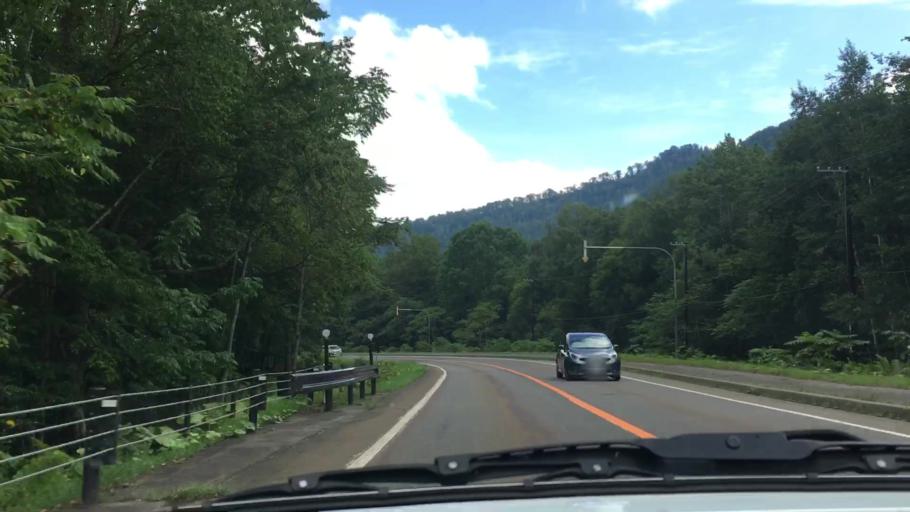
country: JP
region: Hokkaido
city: Otofuke
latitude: 43.3575
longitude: 143.2549
